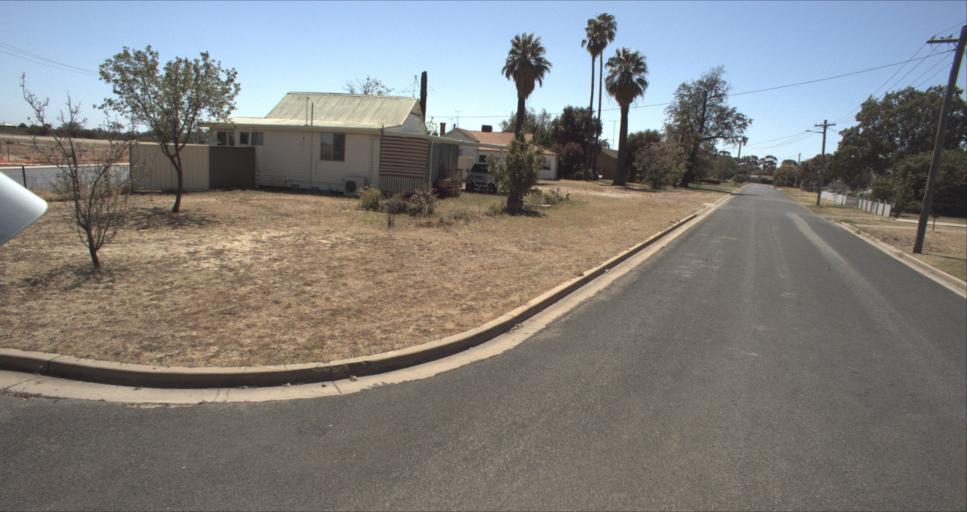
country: AU
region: New South Wales
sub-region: Leeton
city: Leeton
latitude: -34.5451
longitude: 146.3993
